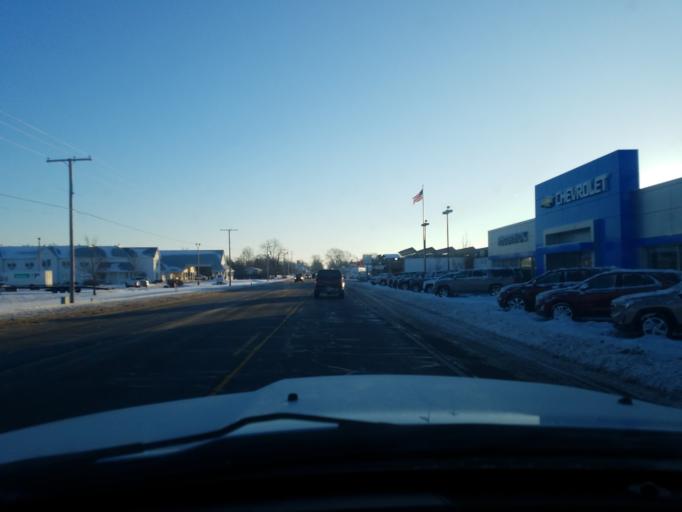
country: US
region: Indiana
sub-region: Elkhart County
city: Nappanee
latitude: 41.4427
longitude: -86.0172
